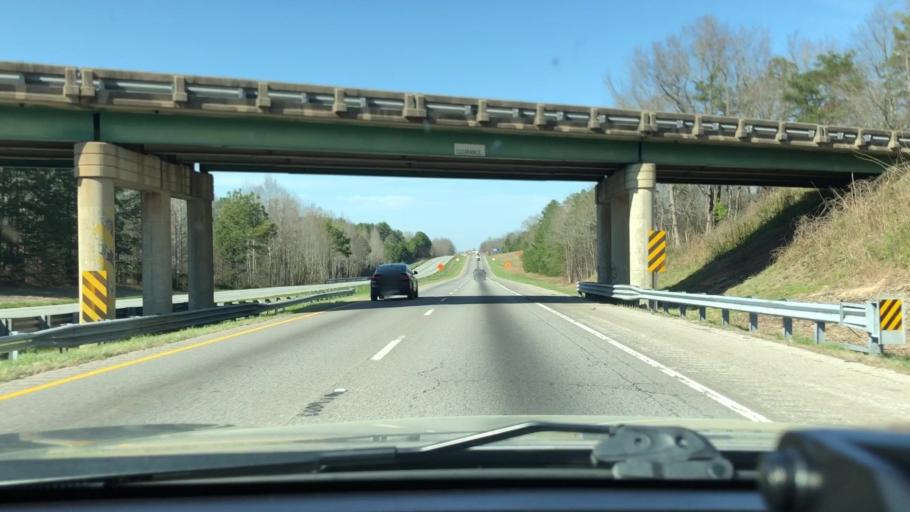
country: US
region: South Carolina
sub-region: Spartanburg County
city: Roebuck
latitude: 34.8978
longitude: -81.9921
